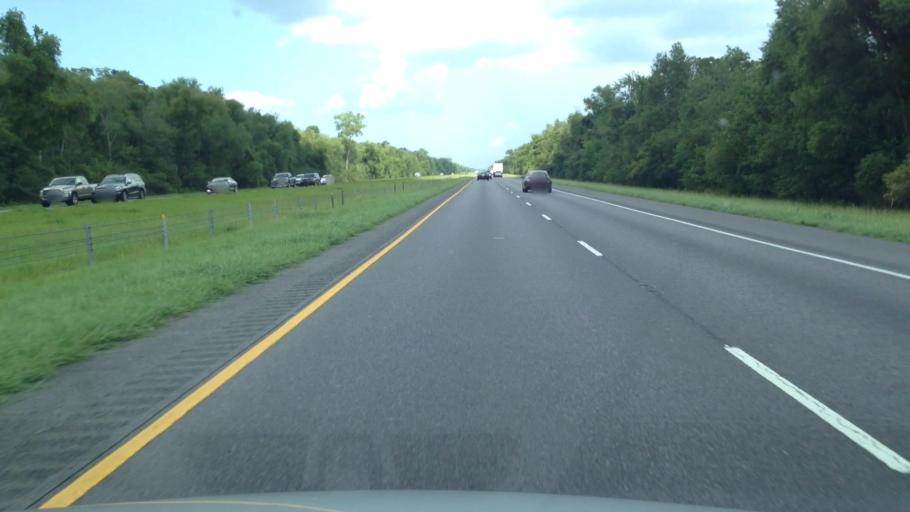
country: US
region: Louisiana
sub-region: Saint James Parish
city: Grand Point
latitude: 30.1410
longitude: -90.7509
